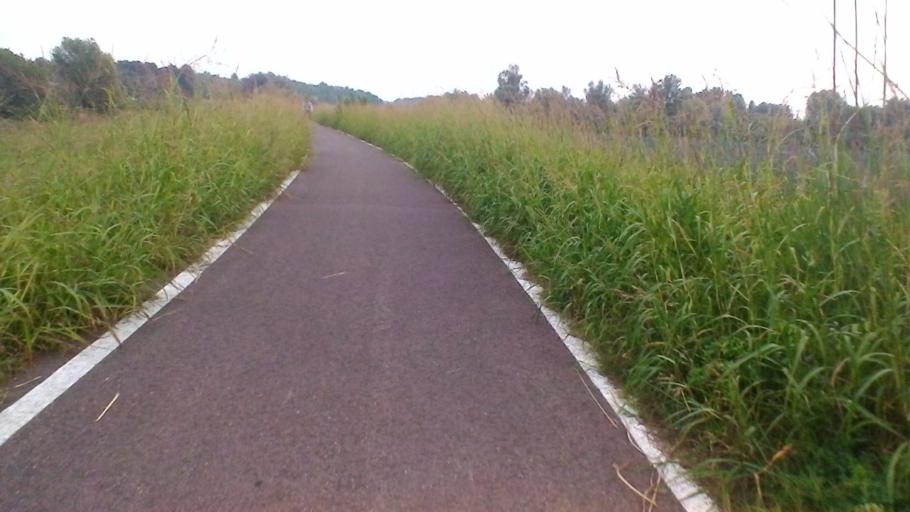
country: IT
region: Veneto
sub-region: Provincia di Verona
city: Zevio
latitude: 45.3827
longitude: 11.1305
